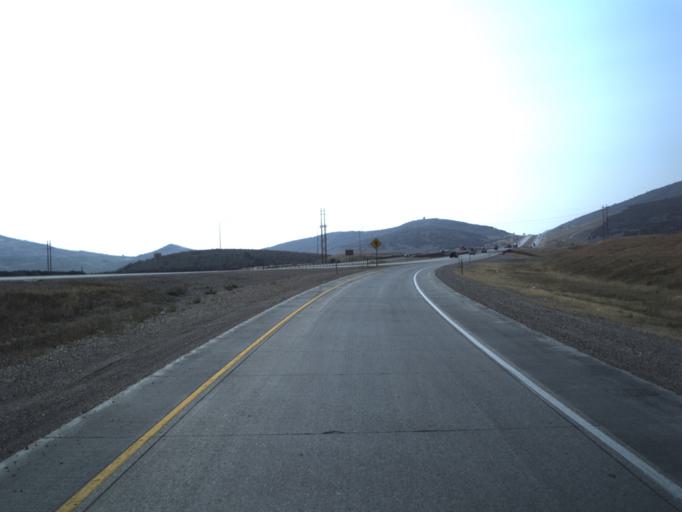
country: US
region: Utah
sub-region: Summit County
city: Park City
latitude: 40.6812
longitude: -111.4622
